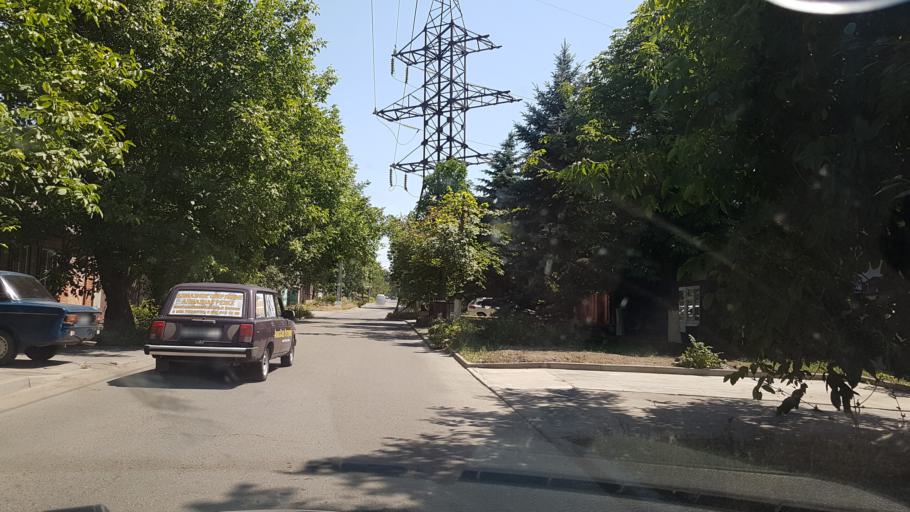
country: RU
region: Rostov
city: Severnyy
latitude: 47.2673
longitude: 39.7120
